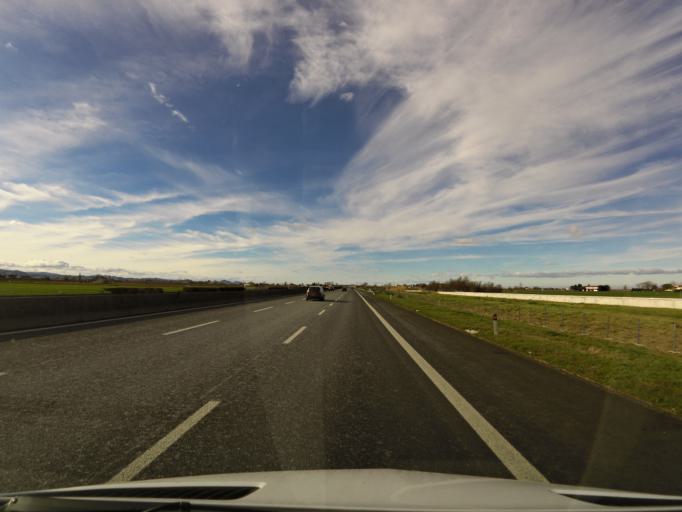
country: IT
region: Emilia-Romagna
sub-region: Forli-Cesena
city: Gambettola
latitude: 44.1364
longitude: 12.3600
